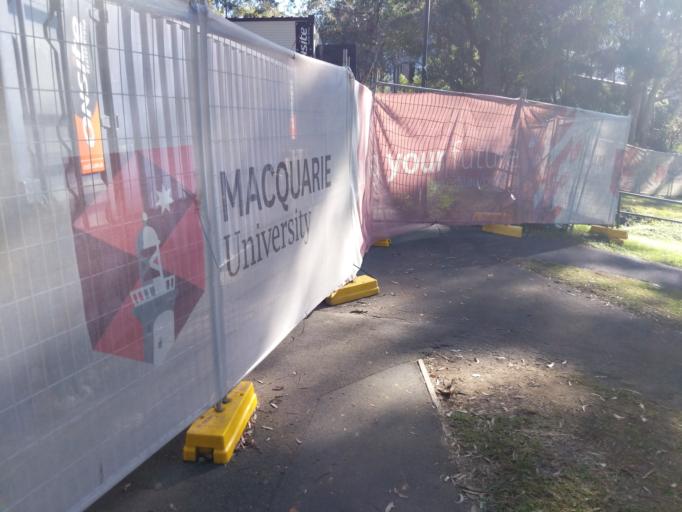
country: AU
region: New South Wales
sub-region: Ryde
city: Macquarie Park
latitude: -33.7760
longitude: 151.1174
